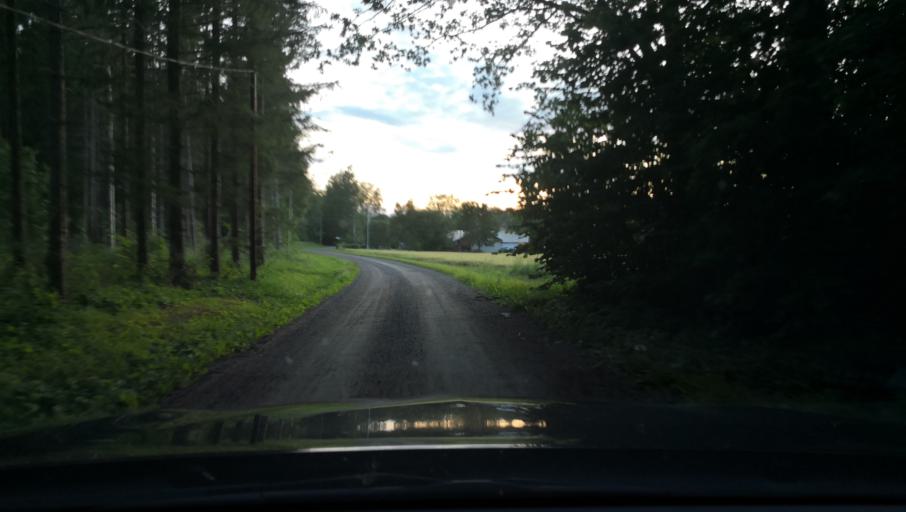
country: SE
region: Uppsala
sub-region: Osthammars Kommun
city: Bjorklinge
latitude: 60.0556
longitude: 17.6103
